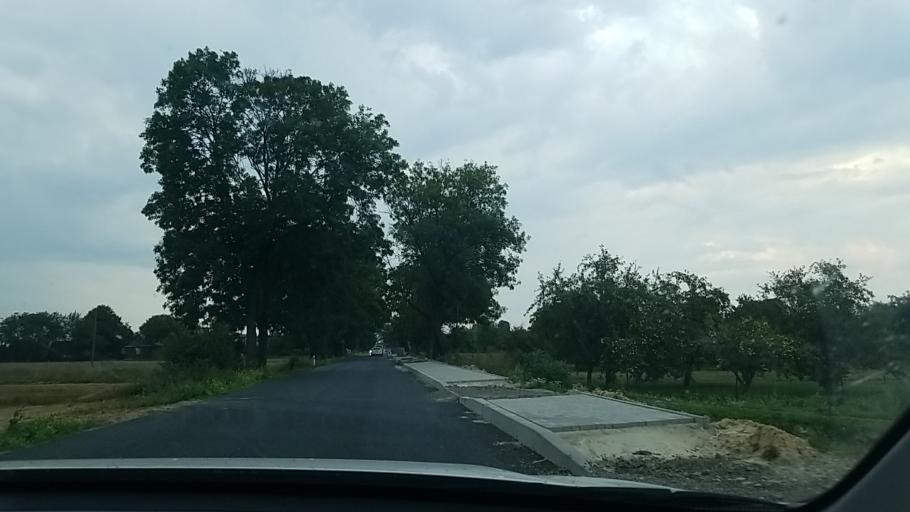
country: PL
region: Lublin Voivodeship
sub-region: Powiat swidnicki
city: Piaski
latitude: 51.1317
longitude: 22.8021
